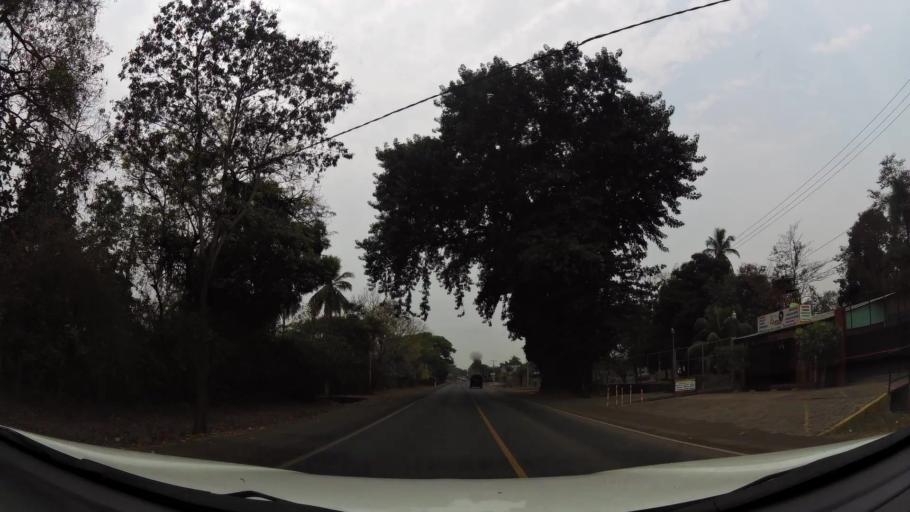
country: NI
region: Chinandega
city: Chinandega
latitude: 12.6142
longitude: -87.0938
